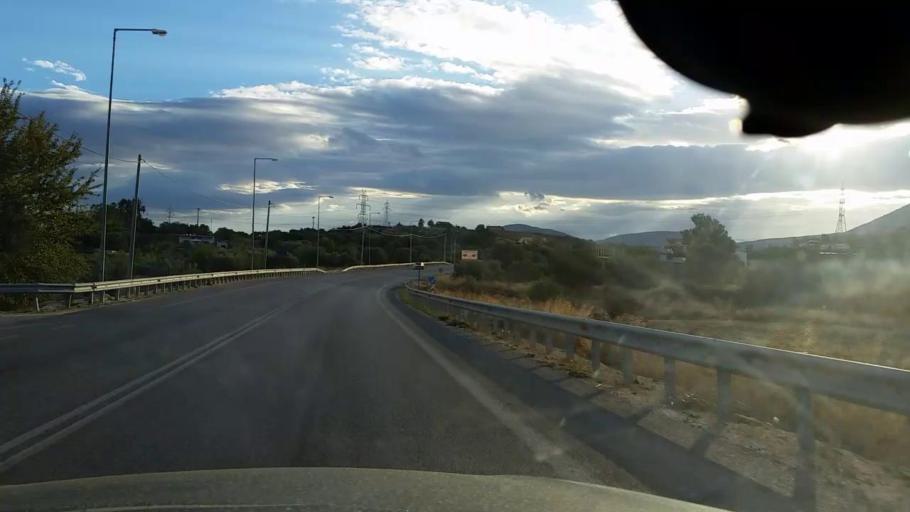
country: GR
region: Attica
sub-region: Nomarchia Anatolikis Attikis
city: Argithea
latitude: 37.9587
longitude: 23.8942
